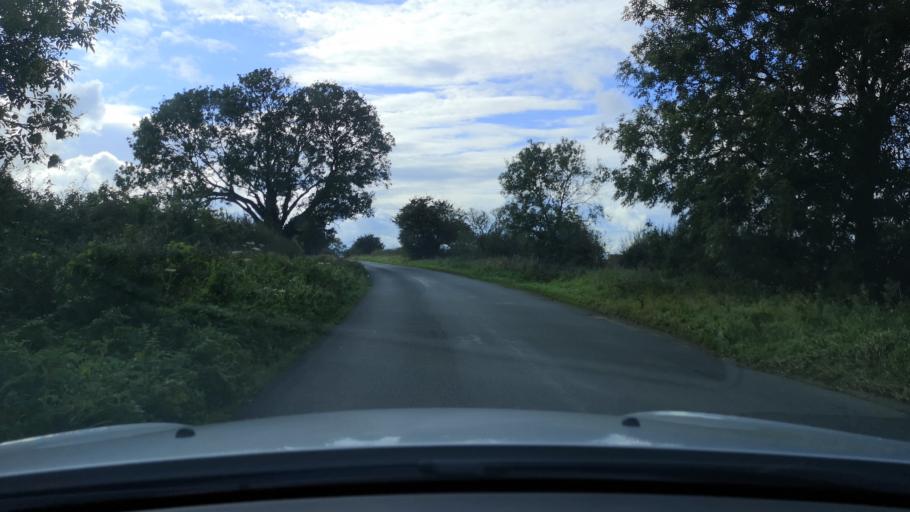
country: GB
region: England
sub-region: East Riding of Yorkshire
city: Walkington
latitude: 53.8327
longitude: -0.4923
